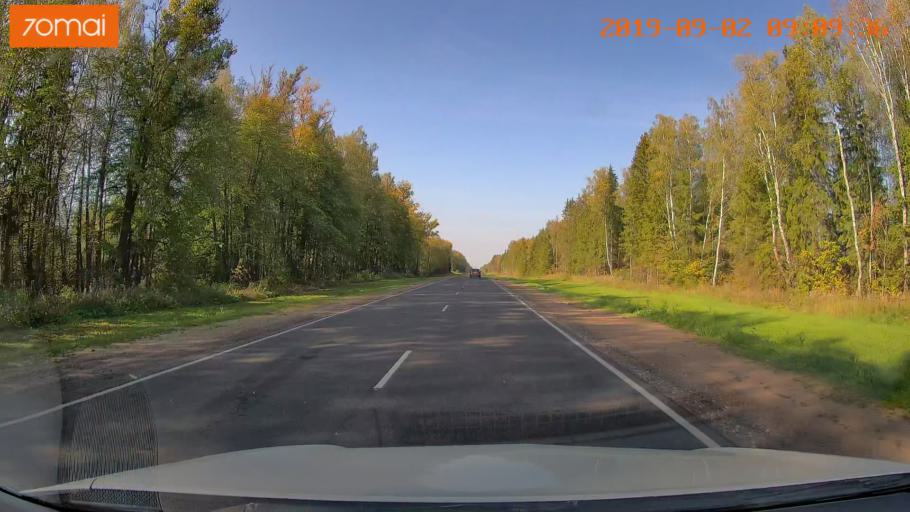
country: RU
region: Kaluga
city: Myatlevo
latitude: 54.8830
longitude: 35.6207
